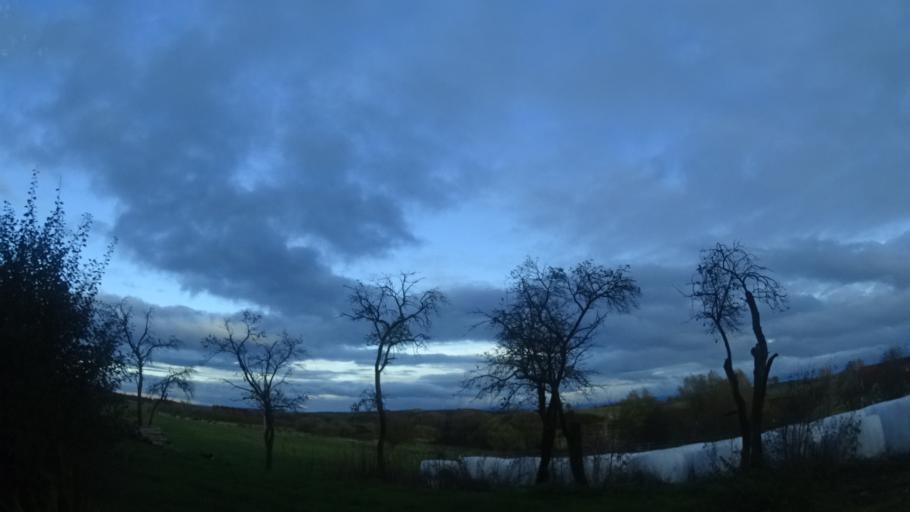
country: DE
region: Hesse
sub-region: Regierungsbezirk Giessen
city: Freiensteinau
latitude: 50.4632
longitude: 9.4049
